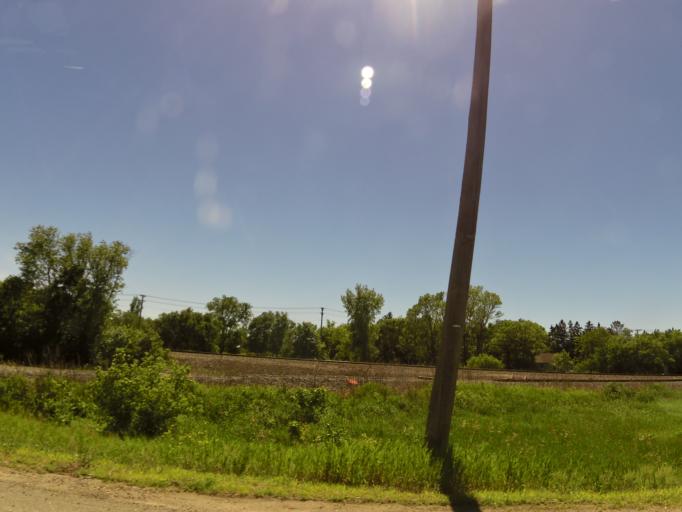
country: US
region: Minnesota
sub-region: Wadena County
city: Wadena
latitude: 46.4401
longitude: -95.1304
